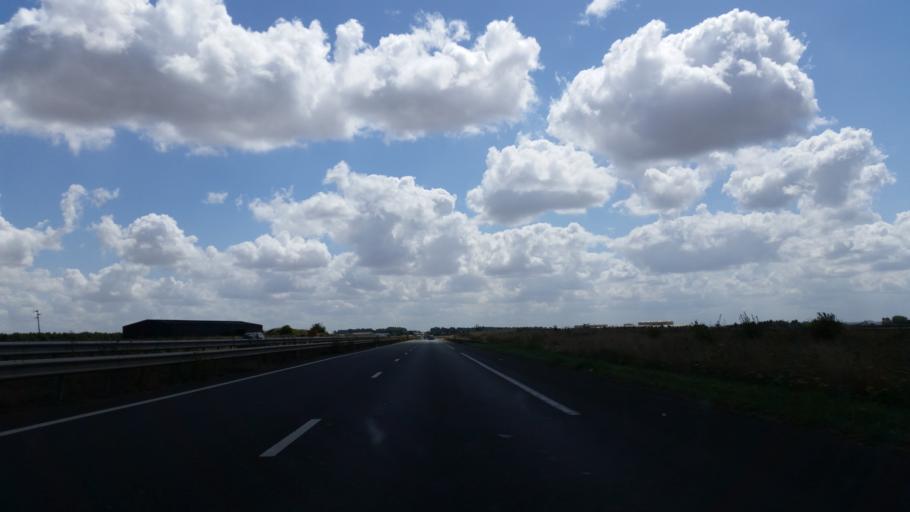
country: FR
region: Lower Normandy
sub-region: Departement du Calvados
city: Bourguebus
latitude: 49.1034
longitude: -0.3148
